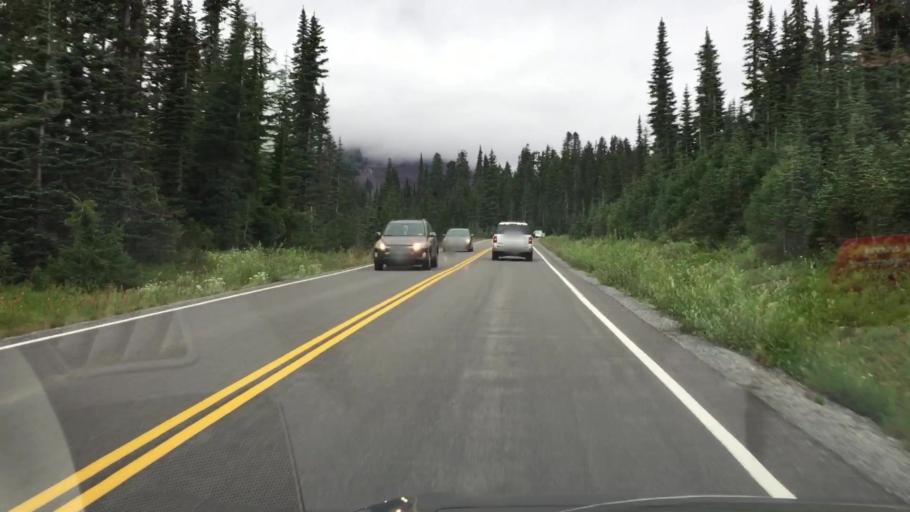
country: US
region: Washington
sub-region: Pierce County
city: Buckley
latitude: 46.7831
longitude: -121.7447
